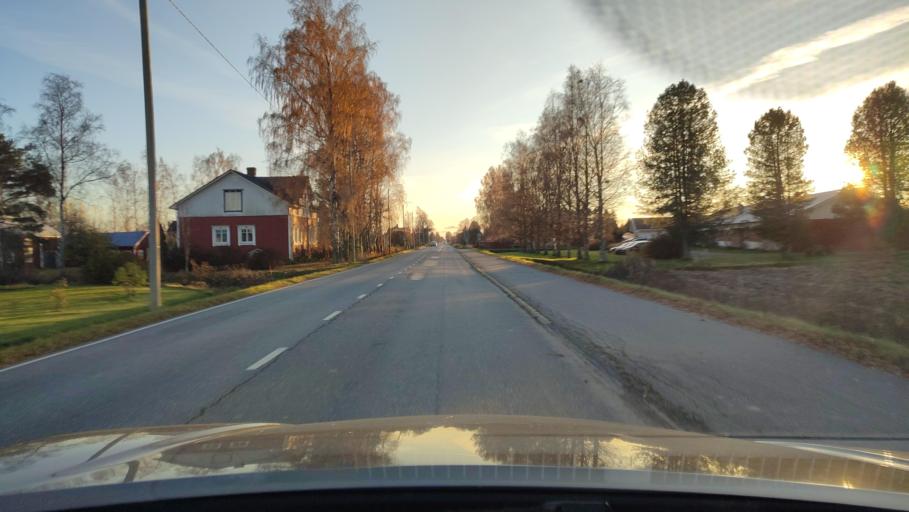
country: FI
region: Ostrobothnia
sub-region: Sydosterbotten
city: Naerpes
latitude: 62.5414
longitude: 21.3928
